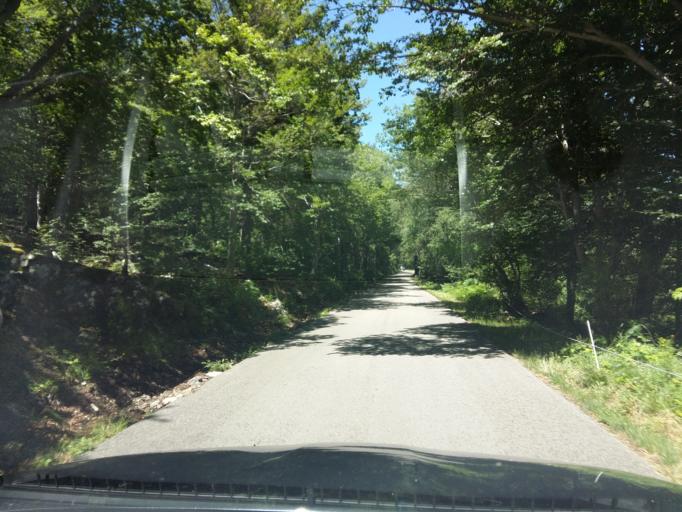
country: ES
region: Castille and Leon
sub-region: Provincia de Soria
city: Vozmediano
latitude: 41.8036
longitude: -1.8123
